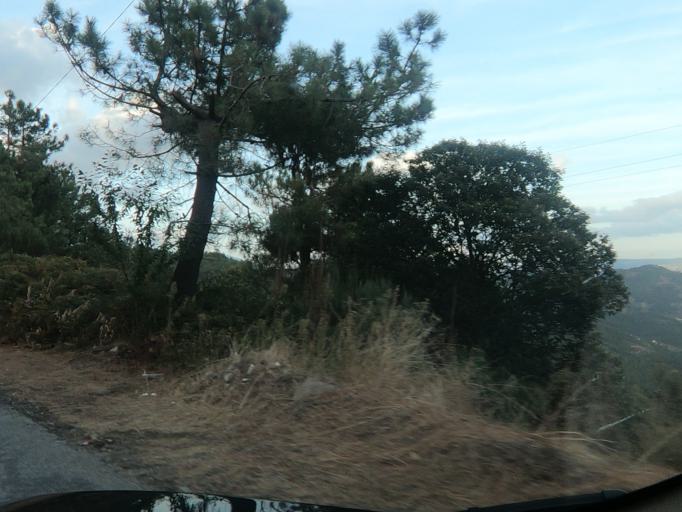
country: PT
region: Vila Real
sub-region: Santa Marta de Penaguiao
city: Santa Marta de Penaguiao
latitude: 41.2387
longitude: -7.8502
